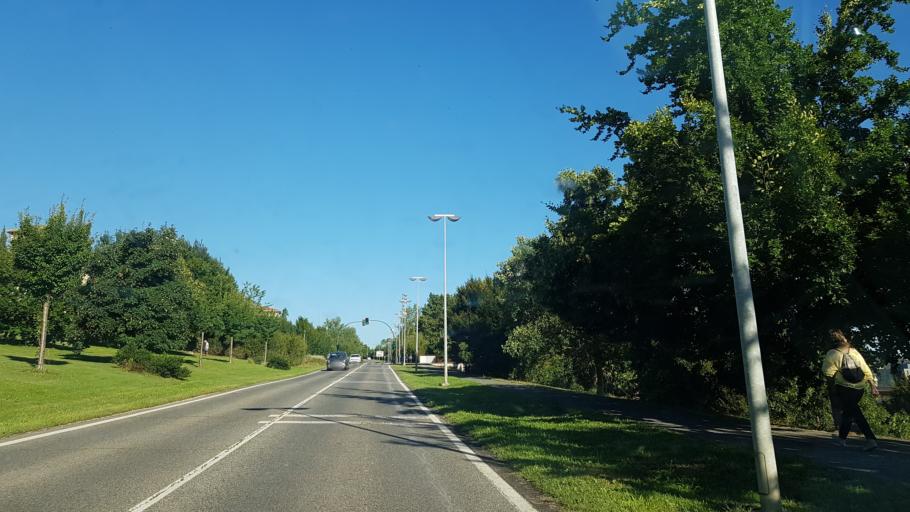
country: ES
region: Navarre
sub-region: Provincia de Navarra
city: Burlata
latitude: 42.8105
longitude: -1.6138
